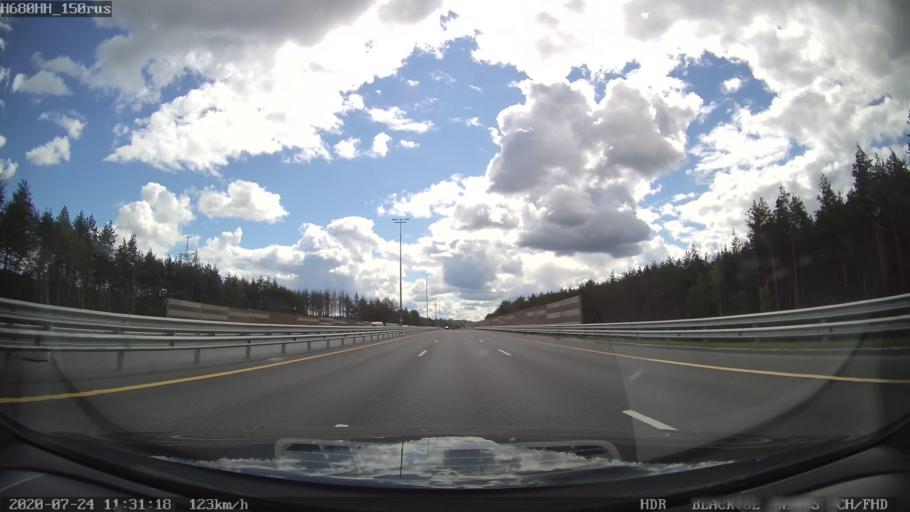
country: RU
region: Leningrad
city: Krasnyy Bor
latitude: 59.6580
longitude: 30.6346
